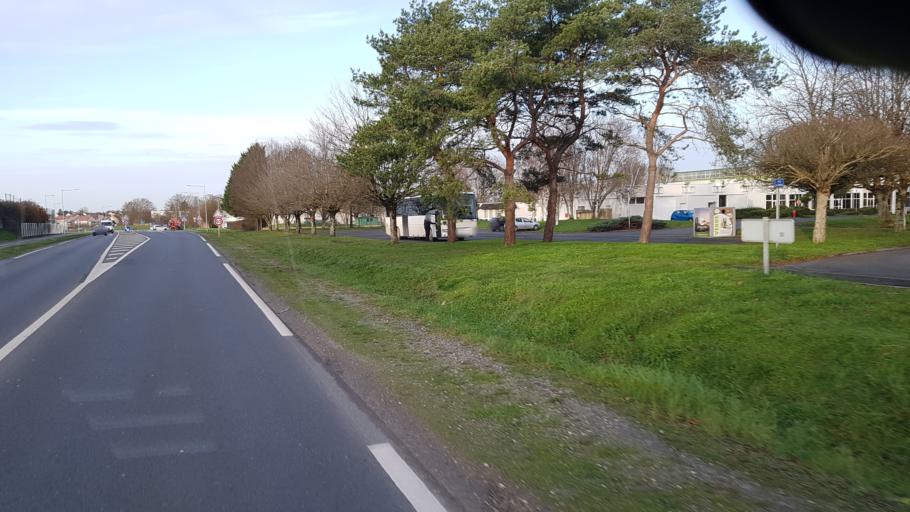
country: FR
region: Centre
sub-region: Departement de l'Indre
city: Chateauroux
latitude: 46.7889
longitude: 1.6945
